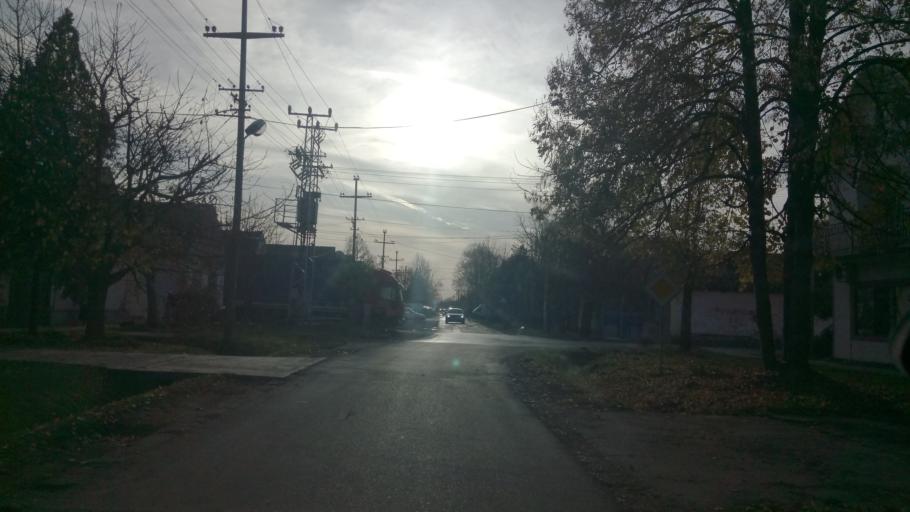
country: RS
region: Autonomna Pokrajina Vojvodina
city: Nova Pazova
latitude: 44.9416
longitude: 20.2280
